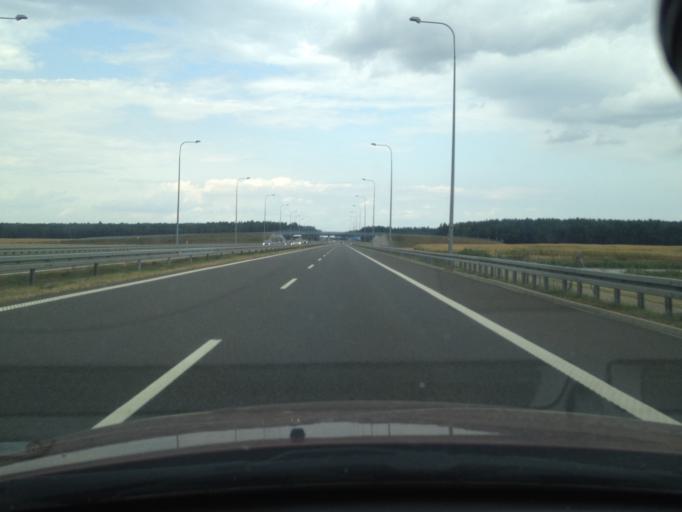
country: PL
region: West Pomeranian Voivodeship
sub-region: Powiat pyrzycki
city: Bielice
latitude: 53.1454
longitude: 14.7169
